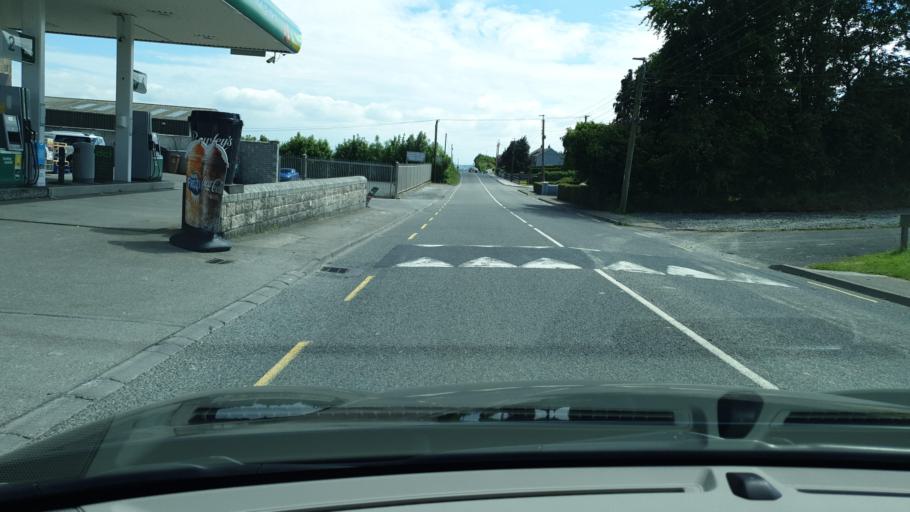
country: IE
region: Ulster
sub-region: An Cabhan
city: Kingscourt
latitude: 53.9002
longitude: -6.8034
